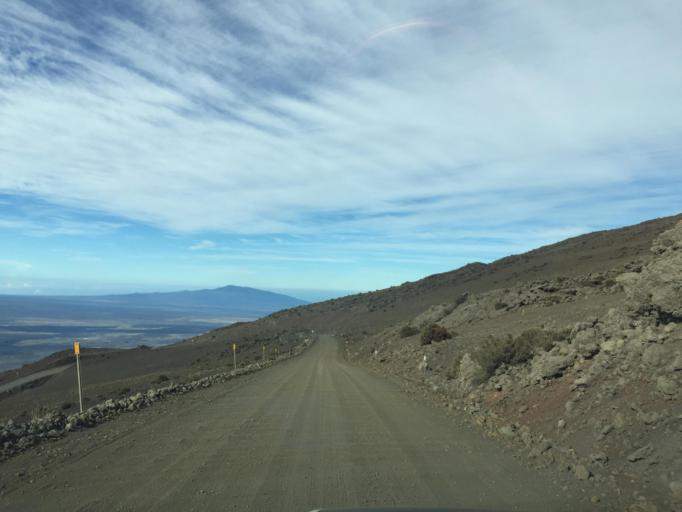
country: US
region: Hawaii
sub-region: Hawaii County
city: Honoka'a
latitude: 19.7705
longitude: -155.4596
